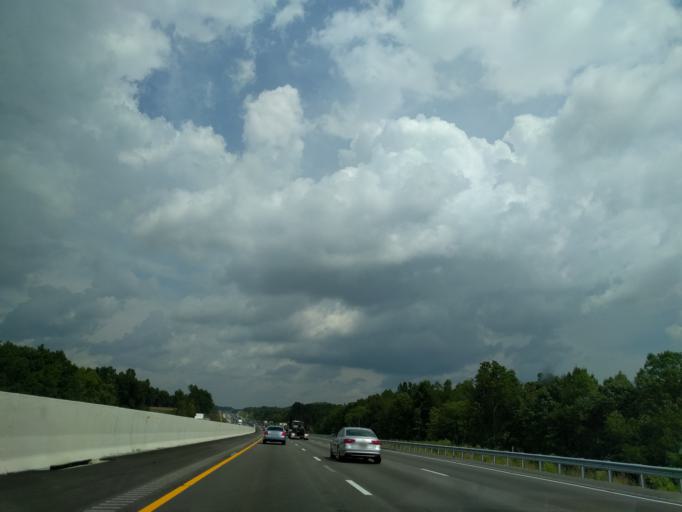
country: US
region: Kentucky
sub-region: Hart County
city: Munfordville
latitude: 37.4061
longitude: -85.8815
